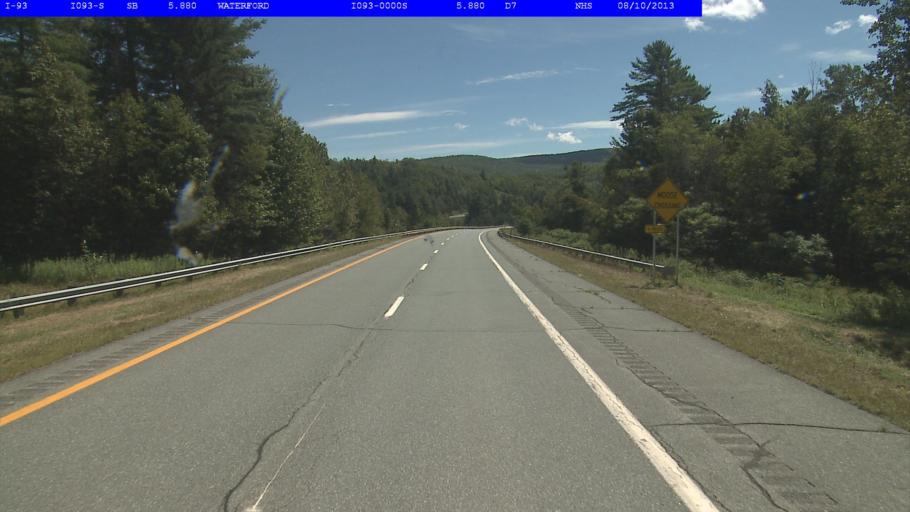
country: US
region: Vermont
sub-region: Caledonia County
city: Saint Johnsbury
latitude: 44.4176
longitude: -71.9297
